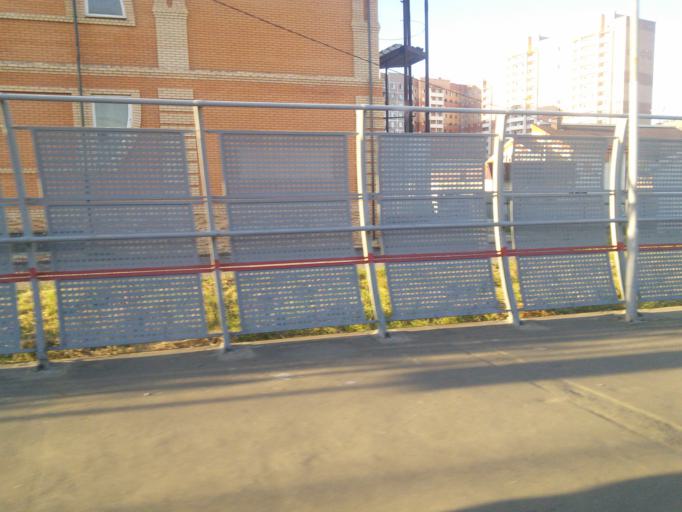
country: RU
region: Moskovskaya
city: Pavlovskiy Posad
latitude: 55.7761
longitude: 38.6732
